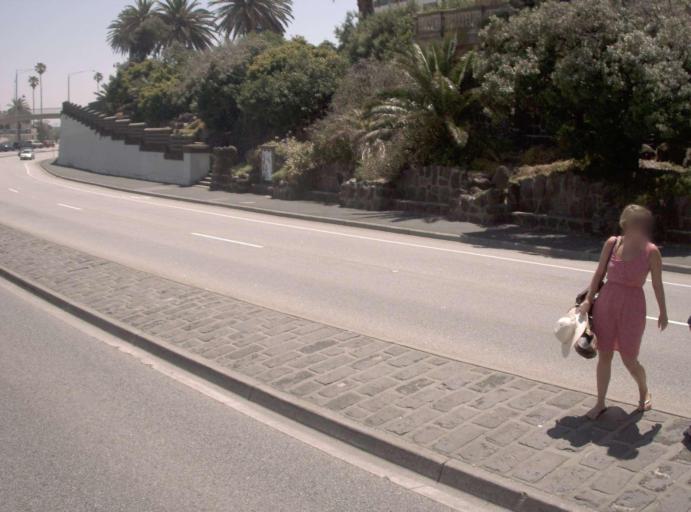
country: AU
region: Victoria
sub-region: Port Phillip
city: St Kilda West
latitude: -37.8653
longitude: 144.9729
